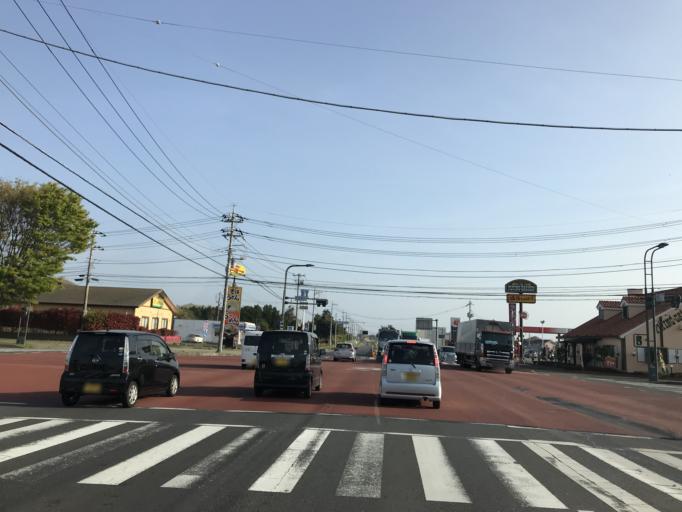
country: JP
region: Ibaraki
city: Hitachi-Naka
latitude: 36.4013
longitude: 140.5805
